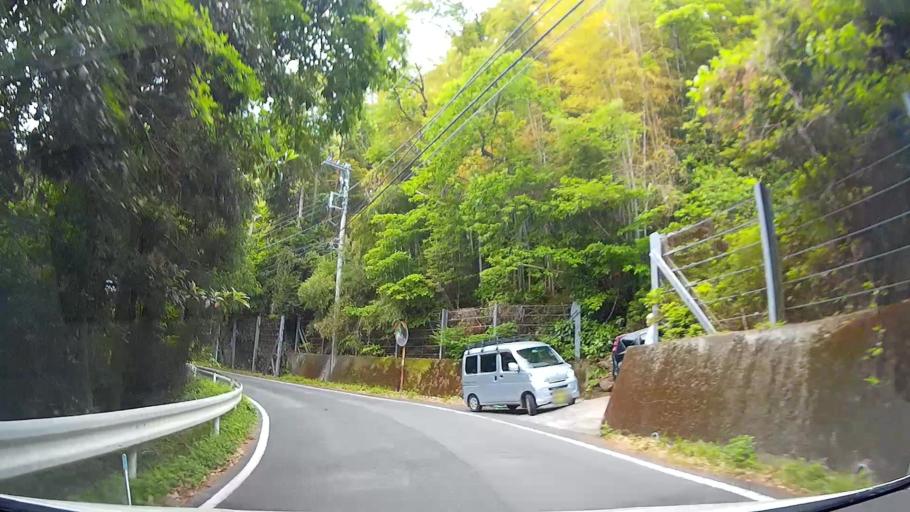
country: JP
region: Shizuoka
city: Ito
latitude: 34.9346
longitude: 139.1379
